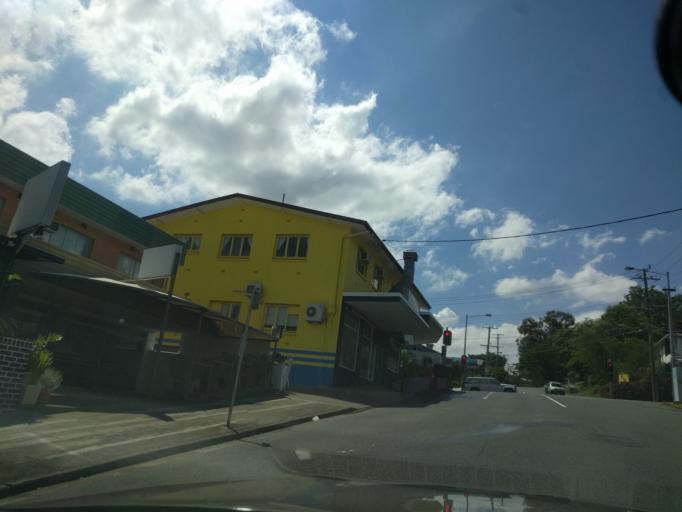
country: AU
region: Queensland
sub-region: Brisbane
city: Milton
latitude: -27.4741
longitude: 152.9961
